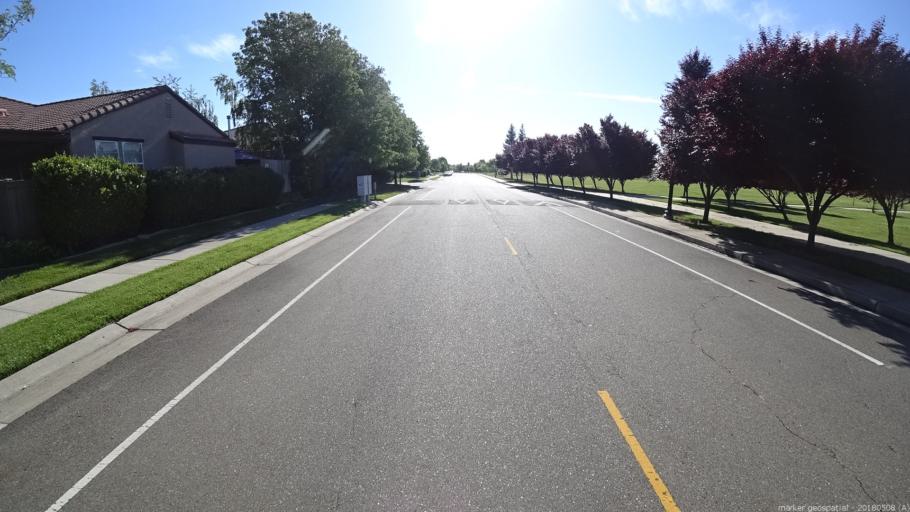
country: US
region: California
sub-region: Sacramento County
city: Elverta
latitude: 38.6761
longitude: -121.5032
